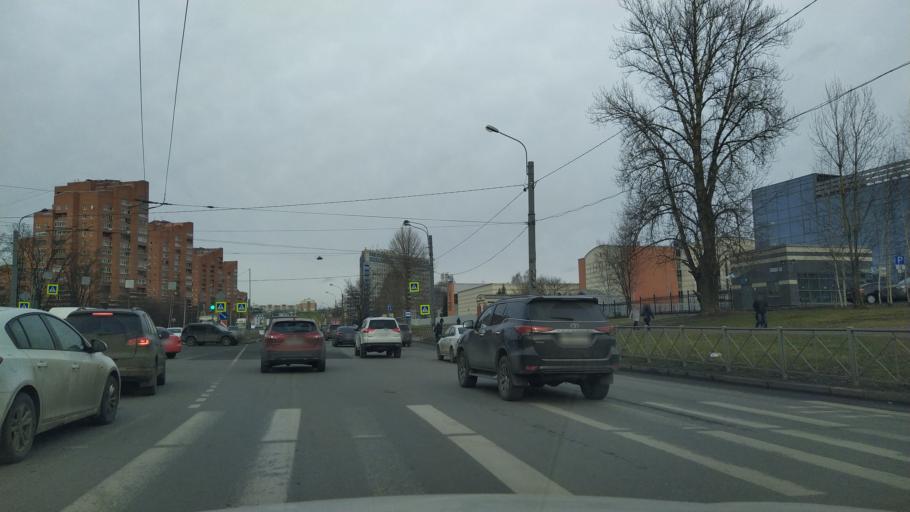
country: RU
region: St.-Petersburg
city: Kolomyagi
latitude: 60.0091
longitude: 30.2960
